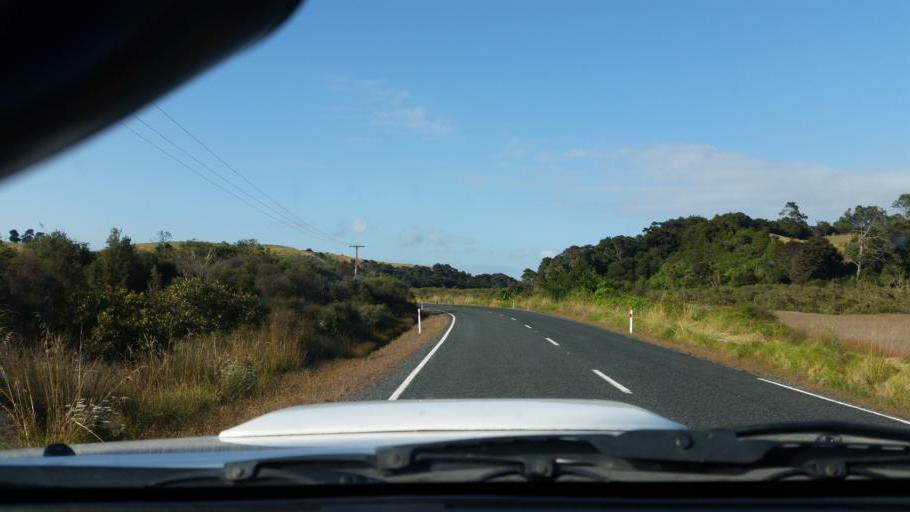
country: NZ
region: Northland
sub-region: Whangarei
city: Ruakaka
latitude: -36.1124
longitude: 174.2299
